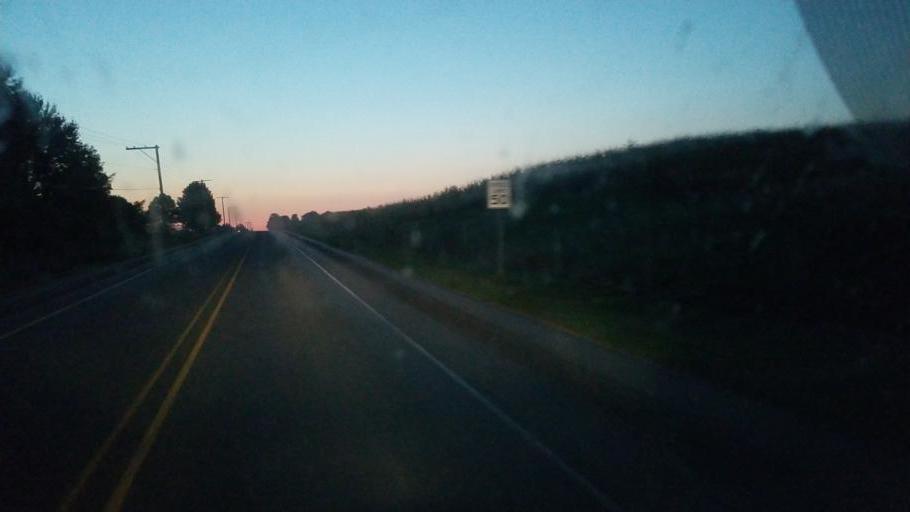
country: US
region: Indiana
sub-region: Elkhart County
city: Middlebury
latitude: 41.6758
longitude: -85.6668
